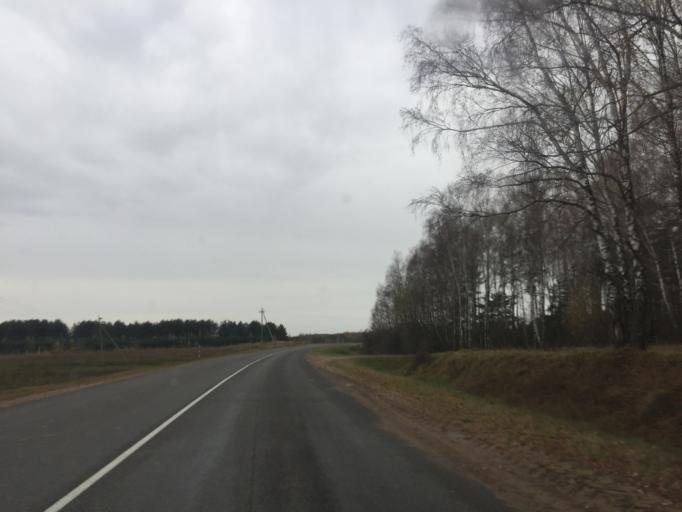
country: BY
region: Mogilev
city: Drybin
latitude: 54.1122
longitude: 31.1250
